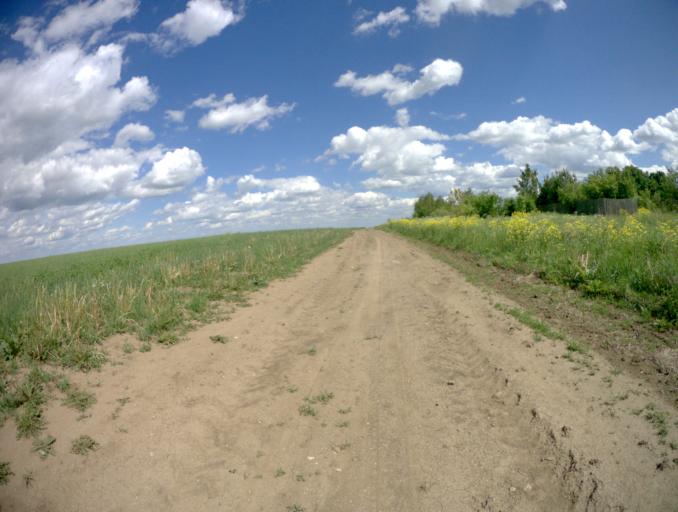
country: RU
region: Vladimir
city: Suzdal'
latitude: 56.4345
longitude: 40.3157
